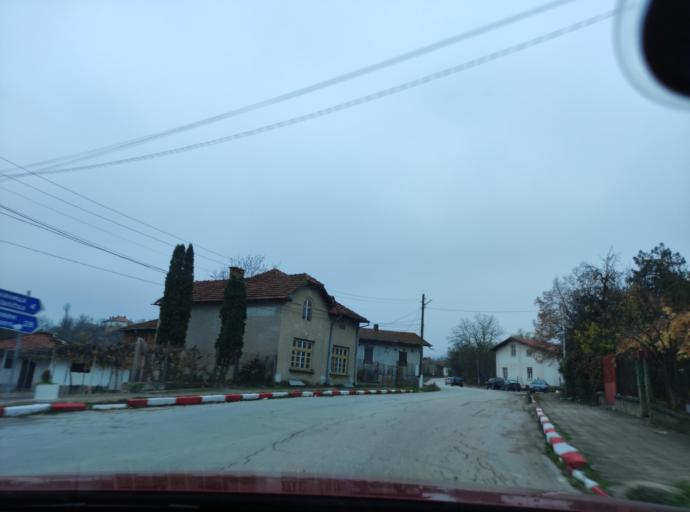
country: BG
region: Lovech
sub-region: Obshtina Yablanitsa
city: Yablanitsa
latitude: 43.0669
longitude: 24.0838
